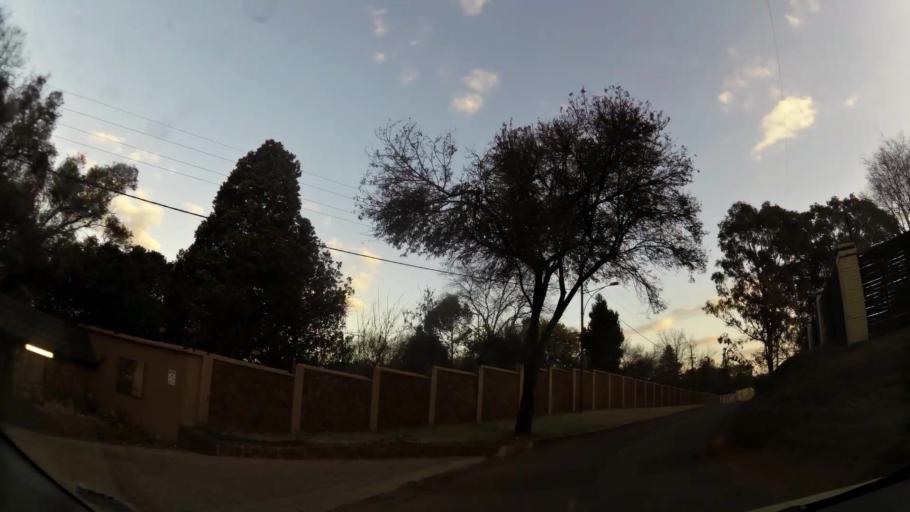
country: ZA
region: Gauteng
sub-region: West Rand District Municipality
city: Krugersdorp
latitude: -26.0676
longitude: 27.7989
